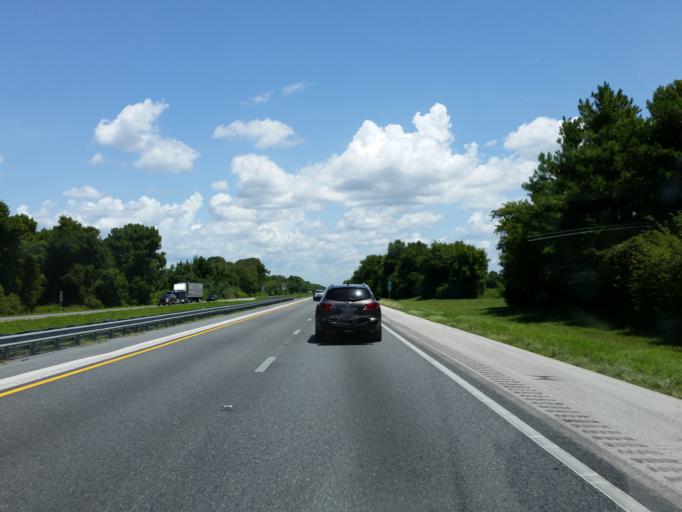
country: US
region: Florida
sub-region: Sumter County
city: Lake Panasoffkee
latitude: 28.8099
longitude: -82.0885
